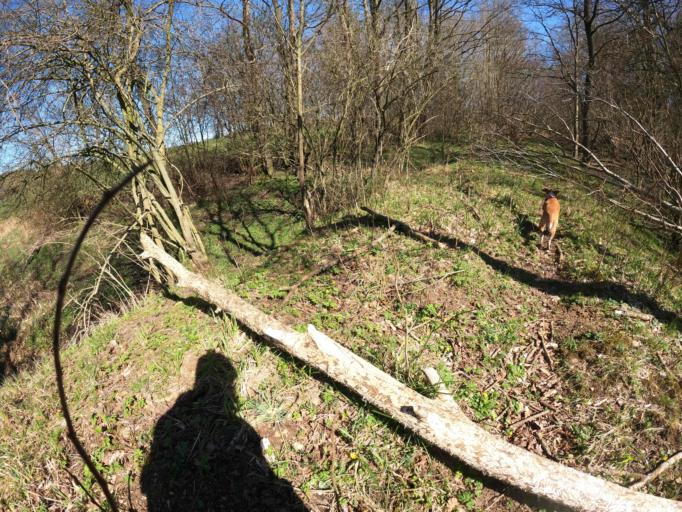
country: PL
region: West Pomeranian Voivodeship
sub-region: Powiat gryficki
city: Gryfice
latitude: 53.9301
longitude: 15.2795
